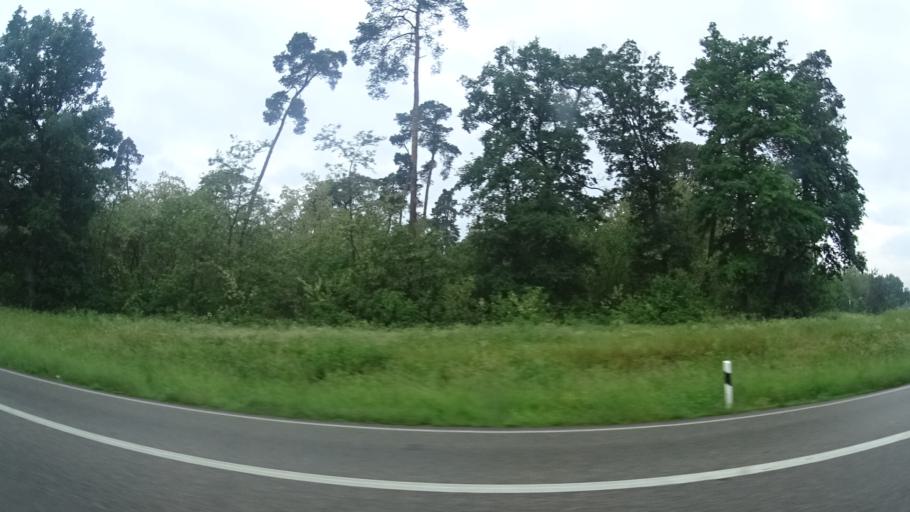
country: DE
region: Rheinland-Pfalz
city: Germersheim
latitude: 49.2056
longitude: 8.3470
